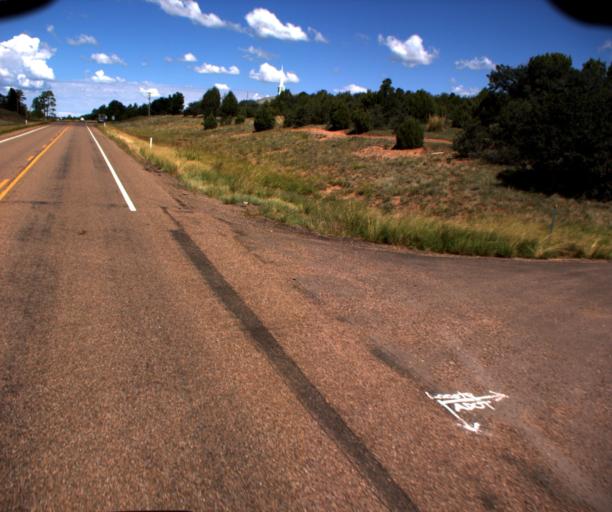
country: US
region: Arizona
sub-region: Navajo County
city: Linden
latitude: 34.3351
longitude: -110.2712
